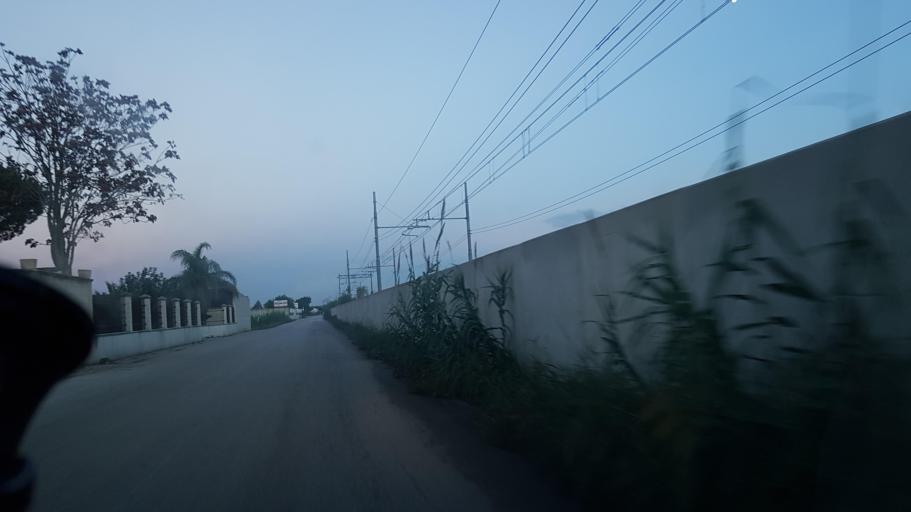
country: IT
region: Apulia
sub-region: Provincia di Brindisi
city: Latiano
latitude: 40.5587
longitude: 17.7236
